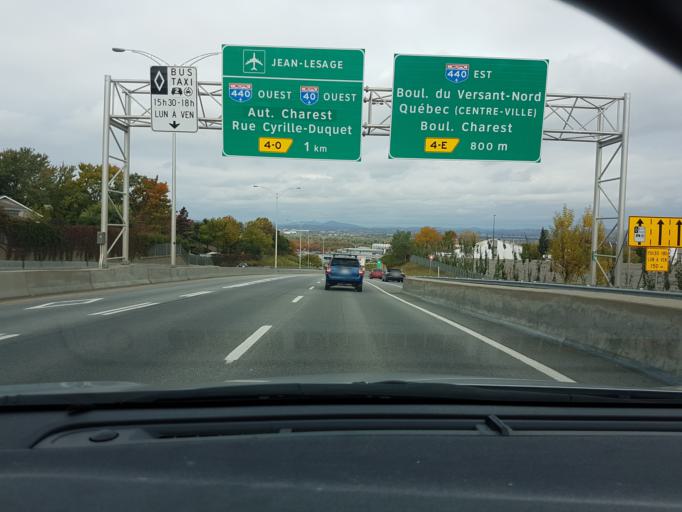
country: CA
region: Quebec
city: L'Ancienne-Lorette
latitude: 46.7861
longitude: -71.2890
